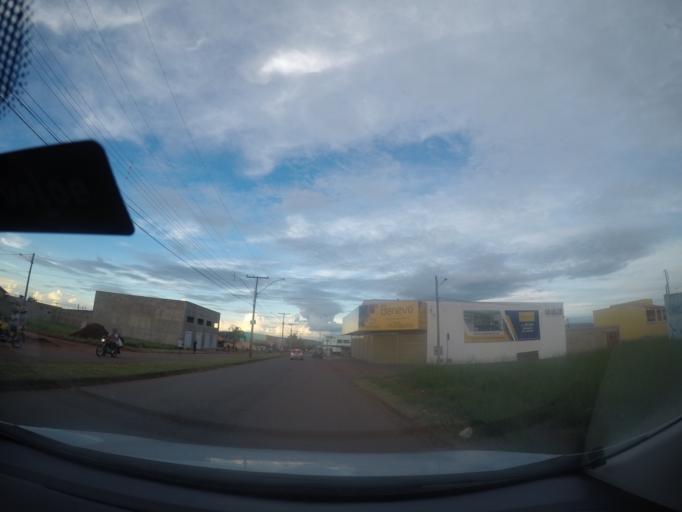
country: BR
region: Goias
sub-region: Goianira
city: Goianira
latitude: -16.5772
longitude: -49.3874
